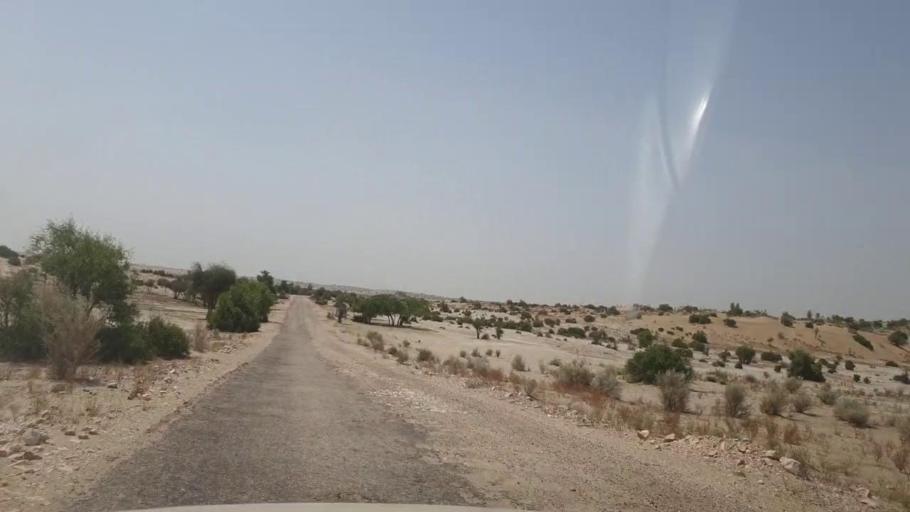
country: PK
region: Sindh
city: Khanpur
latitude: 27.3505
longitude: 69.3182
